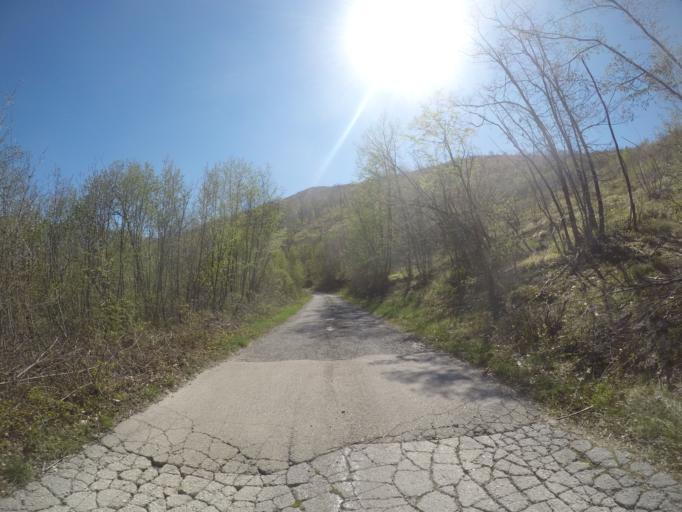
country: ME
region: Danilovgrad
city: Danilovgrad
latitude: 42.5357
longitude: 18.9885
